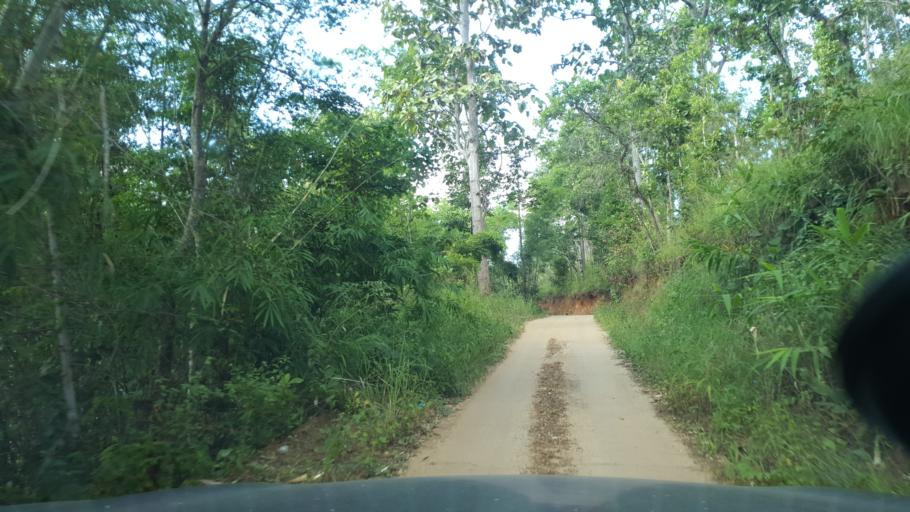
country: TH
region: Chiang Mai
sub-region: Amphoe Chiang Dao
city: Chiang Dao
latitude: 19.4080
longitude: 98.8327
